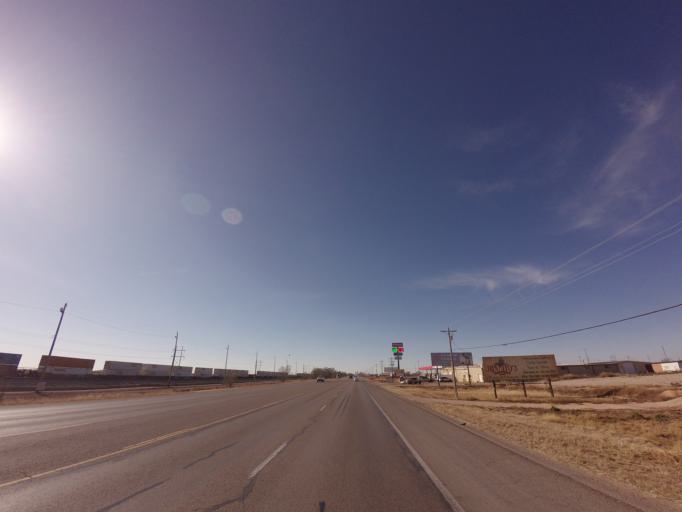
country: US
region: New Mexico
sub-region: Curry County
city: Clovis
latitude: 34.3946
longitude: -103.1512
